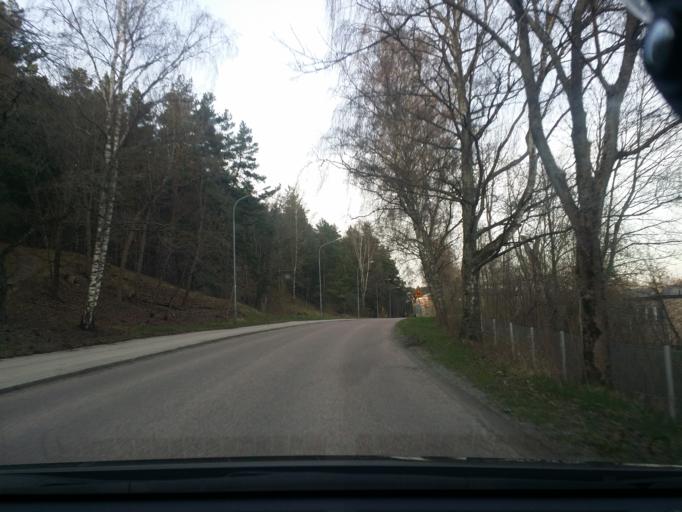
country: SE
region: Uppsala
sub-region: Enkopings Kommun
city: Enkoping
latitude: 59.6401
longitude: 17.0881
